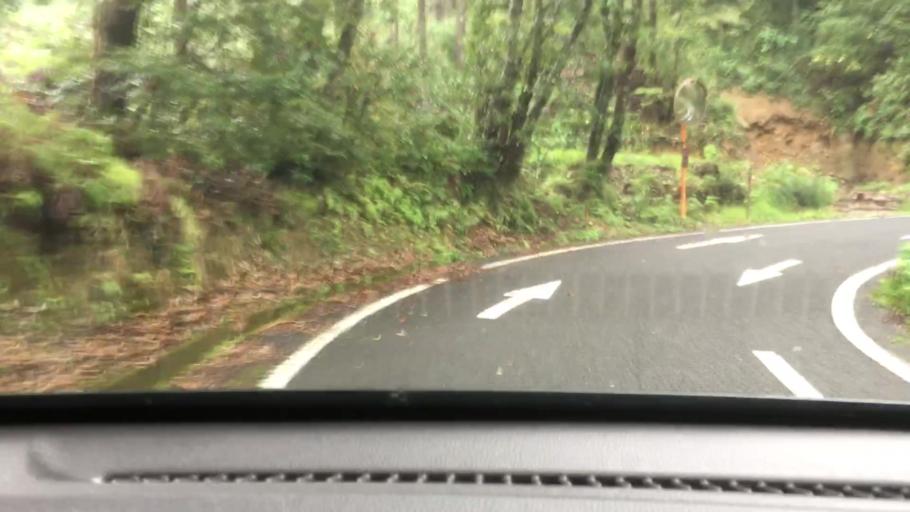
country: JP
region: Nagasaki
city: Togitsu
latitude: 32.9178
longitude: 129.7263
